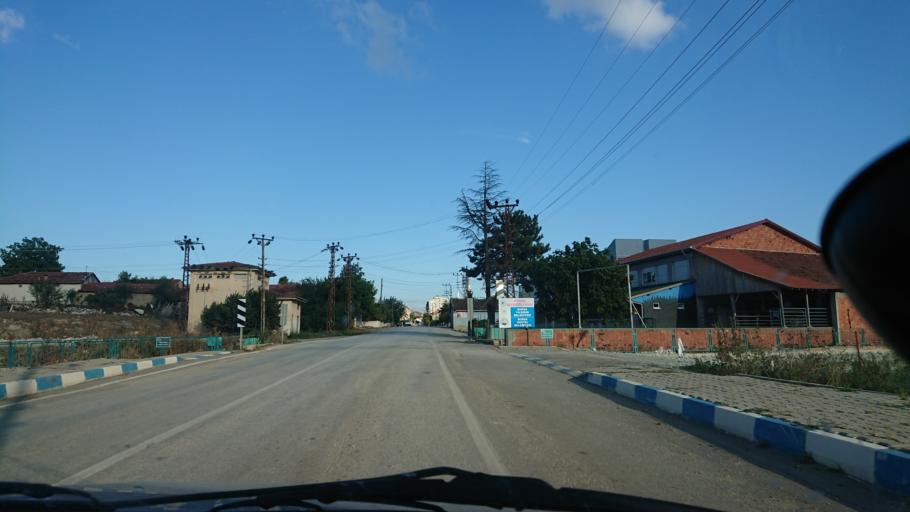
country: TR
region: Bilecik
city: Pazaryeri
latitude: 39.9988
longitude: 29.8919
